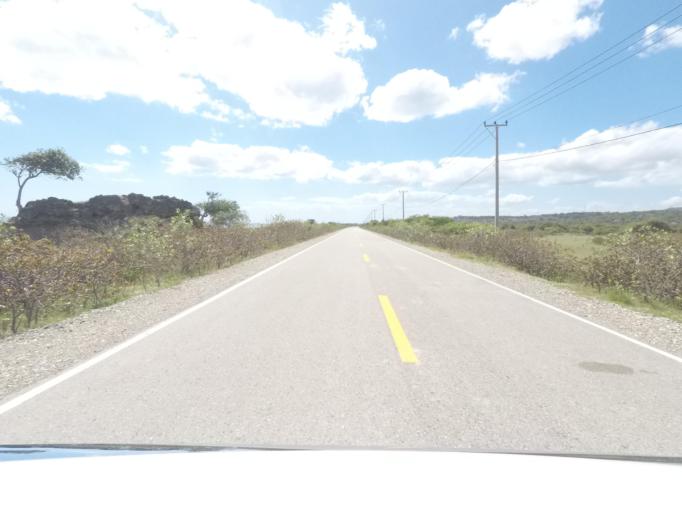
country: TL
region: Baucau
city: Baucau
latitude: -8.4462
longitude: 126.6462
